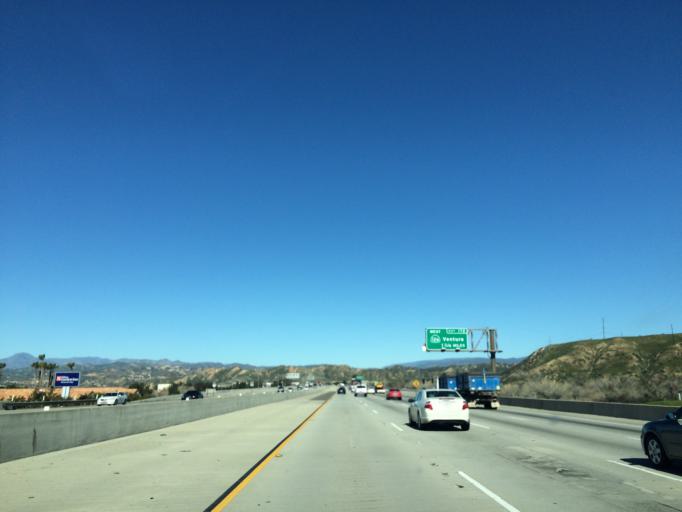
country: US
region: California
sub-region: Los Angeles County
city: Valencia
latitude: 34.4228
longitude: -118.5827
